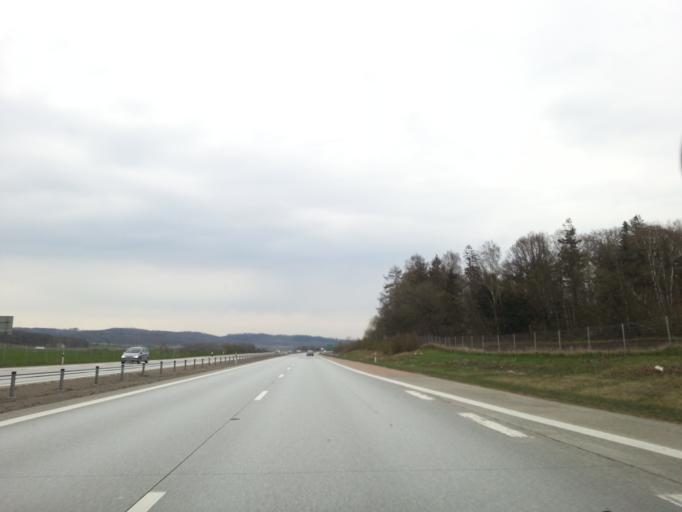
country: SE
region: Halland
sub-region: Halmstads Kommun
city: Getinge
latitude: 56.8054
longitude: 12.7465
